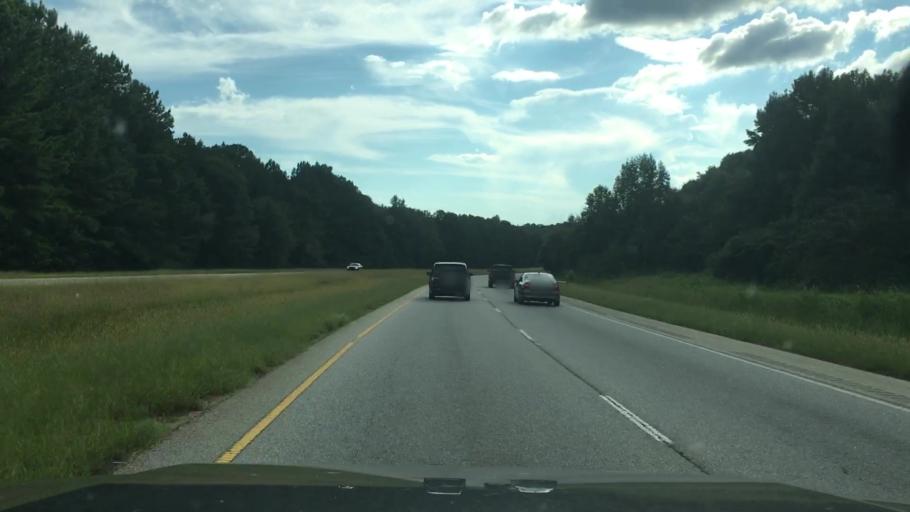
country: US
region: Georgia
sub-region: Spalding County
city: East Griffin
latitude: 33.2378
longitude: -84.1693
